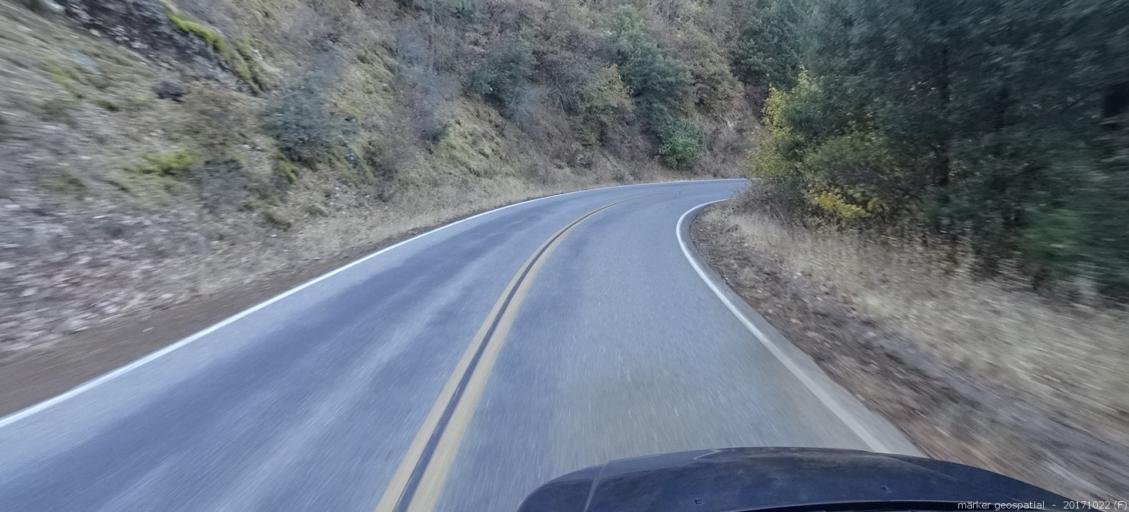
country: US
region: California
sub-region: Shasta County
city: Shasta Lake
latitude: 40.9027
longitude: -122.2341
